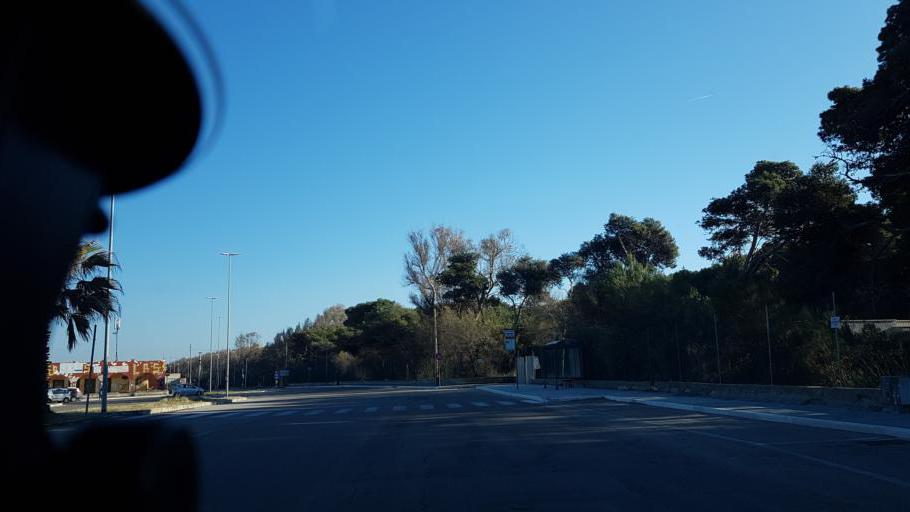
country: IT
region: Apulia
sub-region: Provincia di Lecce
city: Struda
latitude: 40.3840
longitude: 18.3048
